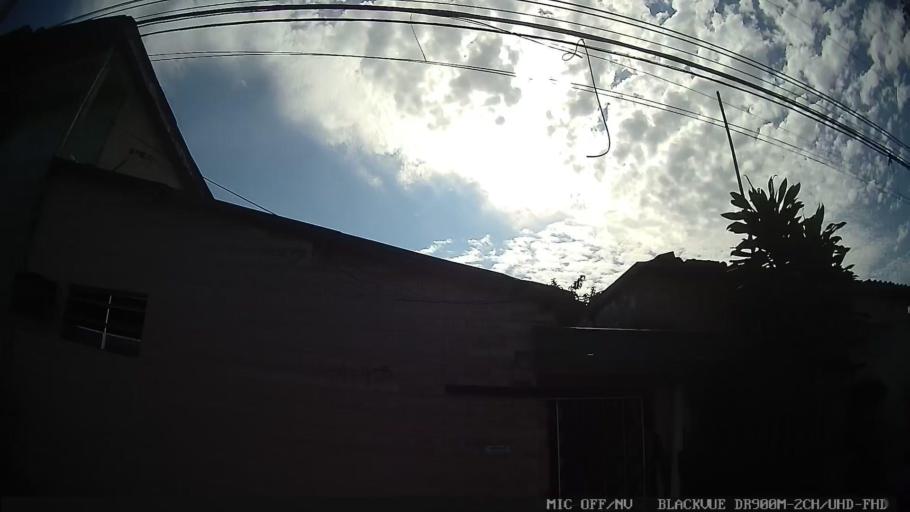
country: BR
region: Sao Paulo
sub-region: Santos
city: Santos
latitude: -23.9453
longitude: -46.2916
